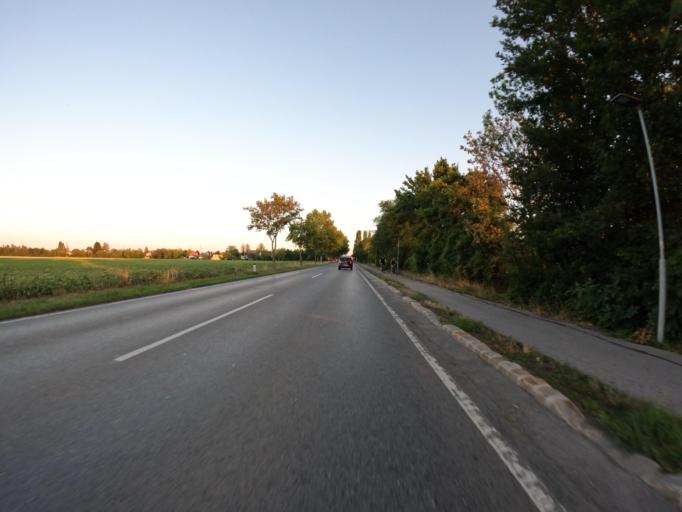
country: AT
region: Lower Austria
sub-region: Politischer Bezirk Baden
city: Pfaffstatten
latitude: 47.9949
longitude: 16.2745
